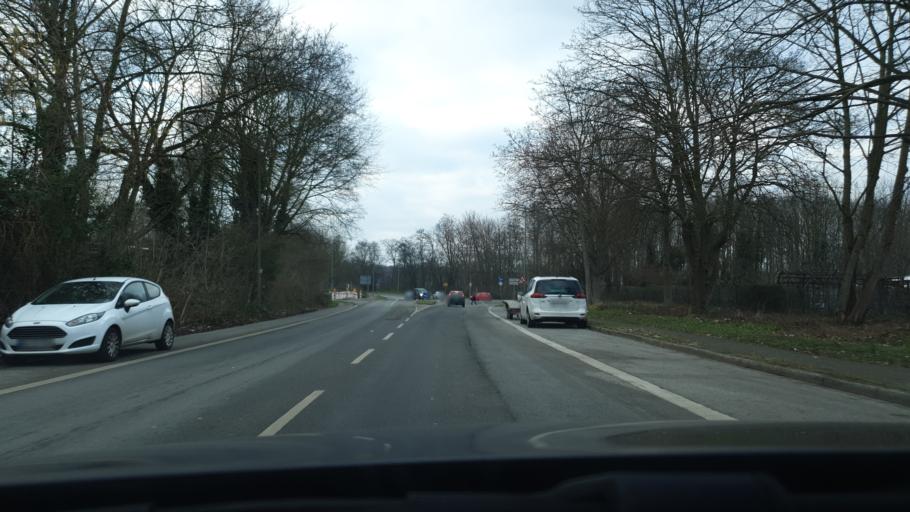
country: DE
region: North Rhine-Westphalia
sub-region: Regierungsbezirk Dusseldorf
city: Hochfeld
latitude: 51.3955
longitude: 6.6890
